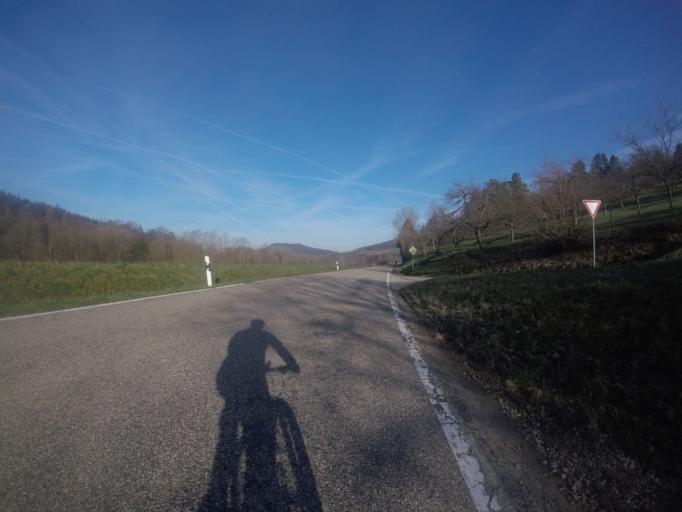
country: DE
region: Baden-Wuerttemberg
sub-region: Regierungsbezirk Stuttgart
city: Oberstenfeld
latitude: 49.0327
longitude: 9.3583
